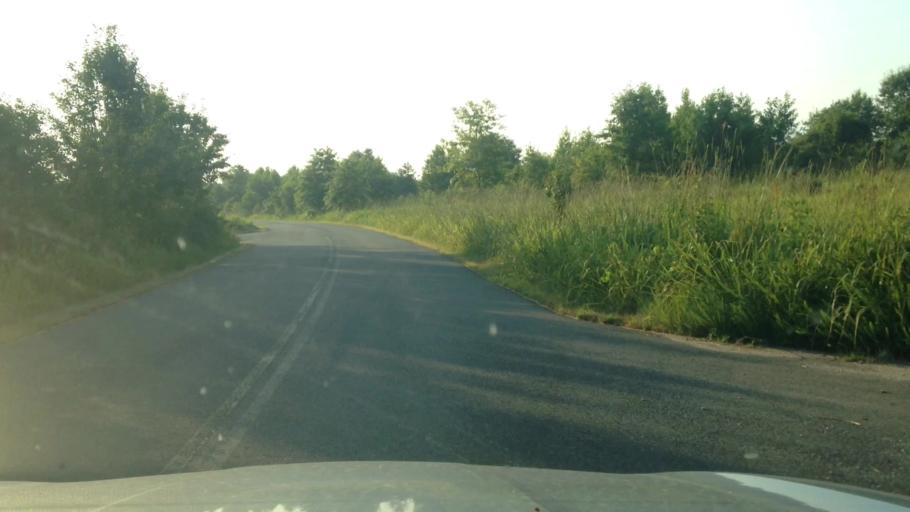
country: US
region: Virginia
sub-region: Prince William County
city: Woodbridge
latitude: 38.6458
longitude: -77.2404
